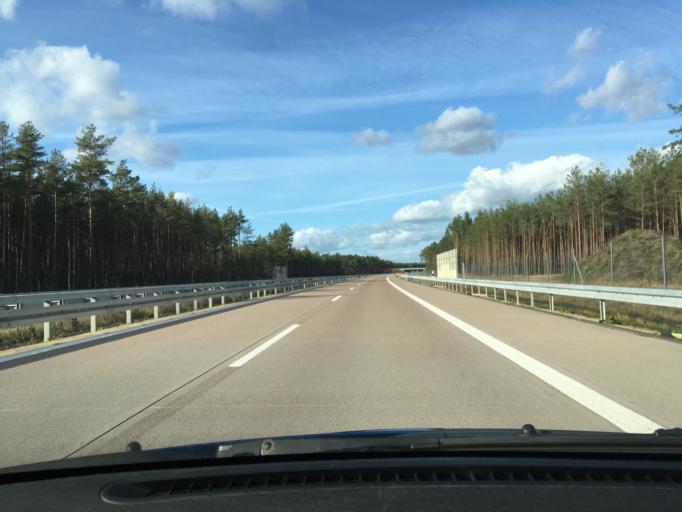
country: DE
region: Mecklenburg-Vorpommern
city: Grabow
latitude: 53.2694
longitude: 11.5299
